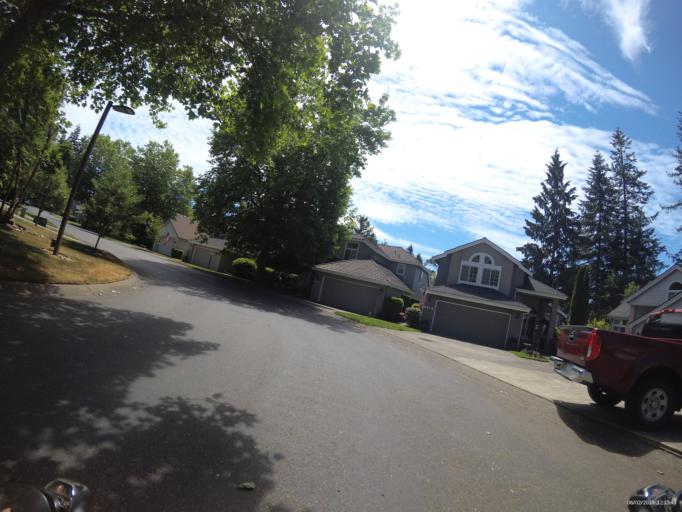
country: US
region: Washington
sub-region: Pierce County
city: University Place
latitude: 47.2016
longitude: -122.5496
